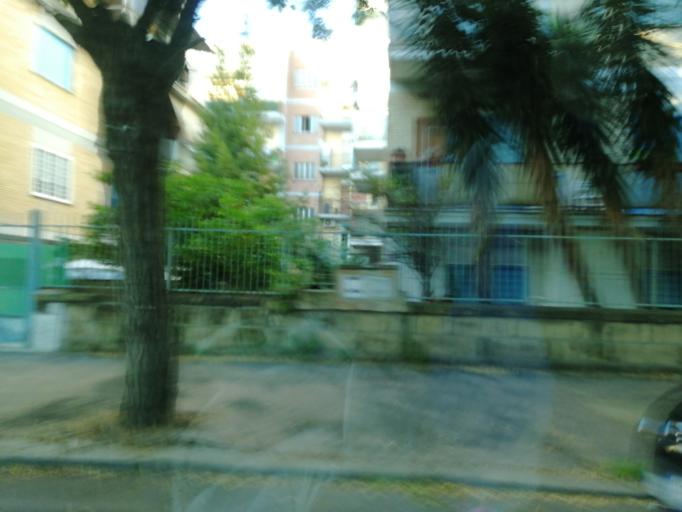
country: IT
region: Latium
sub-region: Citta metropolitana di Roma Capitale
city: Rome
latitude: 41.8616
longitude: 12.5464
